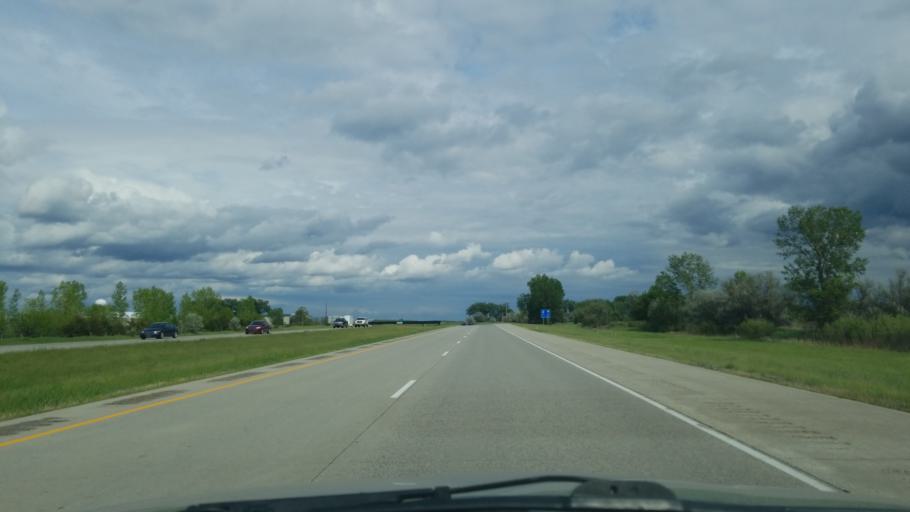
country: US
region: North Dakota
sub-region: Cass County
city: Casselton
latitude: 46.8745
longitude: -97.2296
